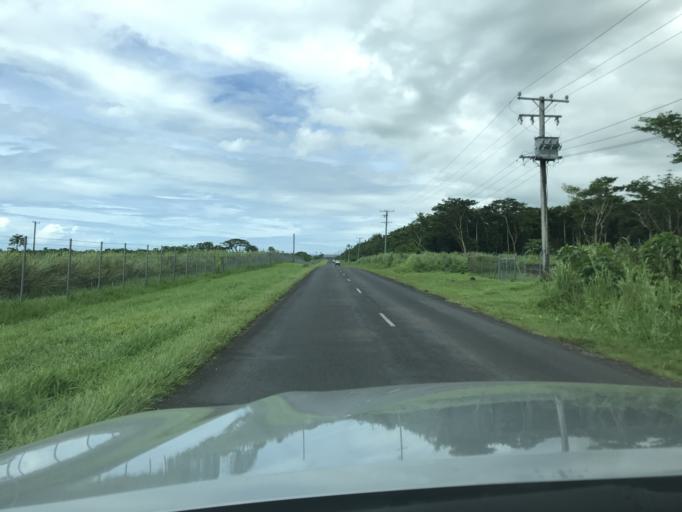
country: WS
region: Aiga-i-le-Tai
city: Mulifanua
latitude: -13.8339
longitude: -172.0125
